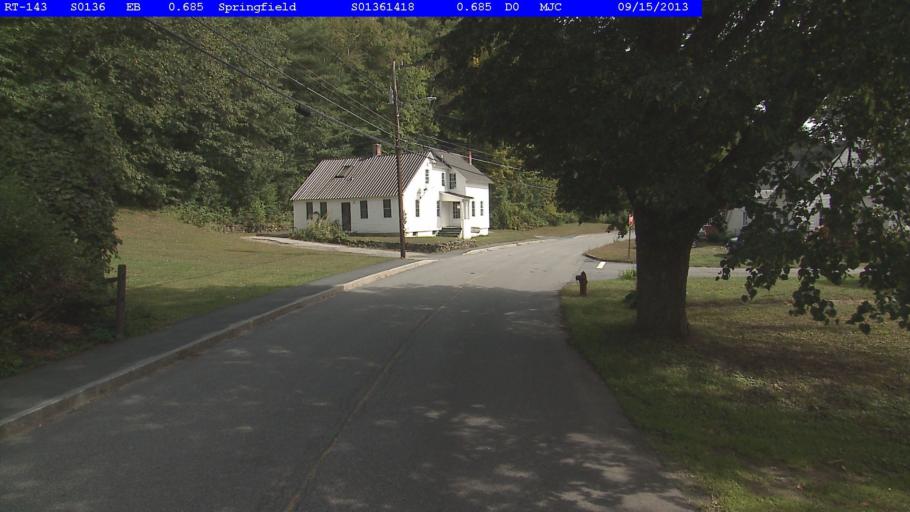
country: US
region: Vermont
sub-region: Windsor County
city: Springfield
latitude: 43.2970
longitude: -72.4699
